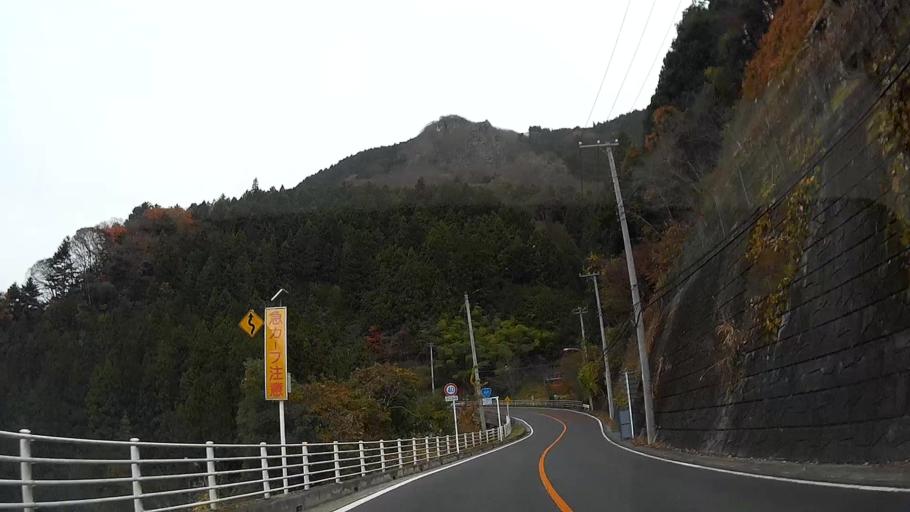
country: JP
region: Saitama
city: Chichibu
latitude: 35.9586
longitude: 138.9030
